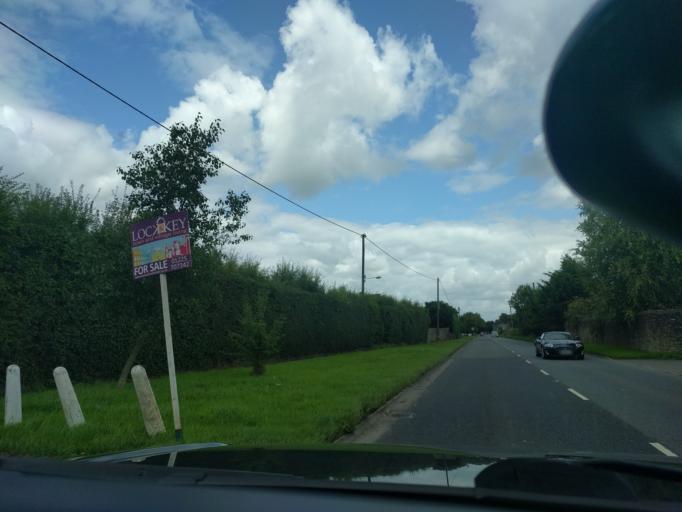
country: GB
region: England
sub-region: Wiltshire
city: Melksham
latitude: 51.3916
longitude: -2.1407
